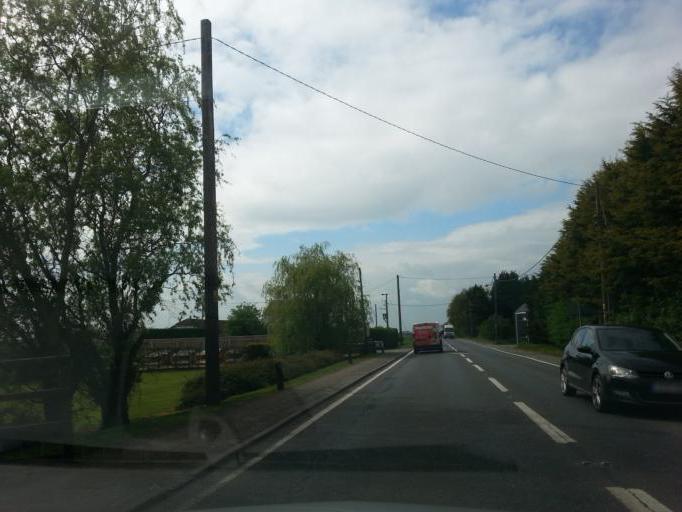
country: GB
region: England
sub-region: Cambridgeshire
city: March
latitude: 52.6075
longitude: 0.0567
